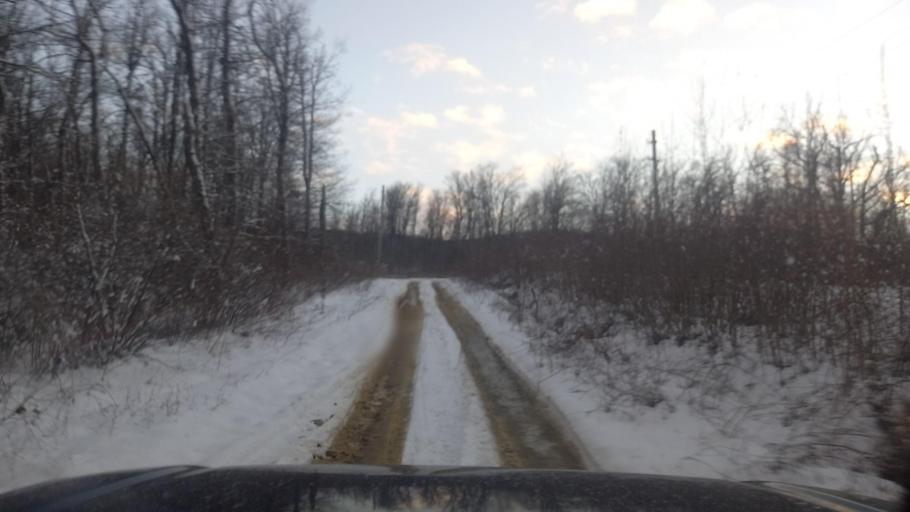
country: RU
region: Krasnodarskiy
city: Smolenskaya
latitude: 44.6715
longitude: 38.7958
